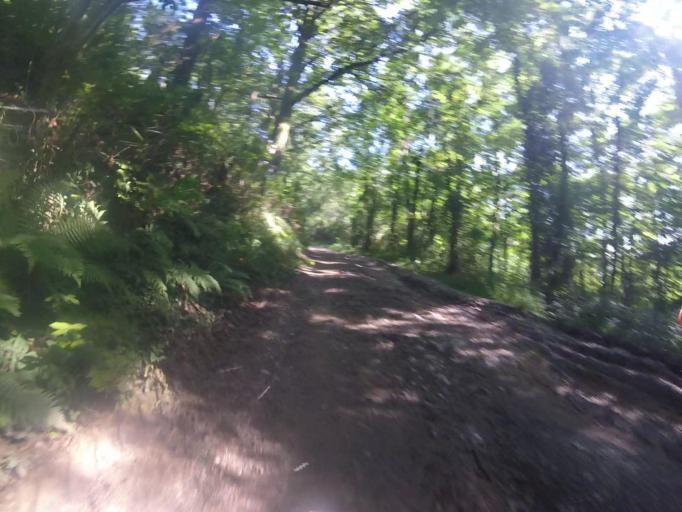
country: ES
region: Basque Country
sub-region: Provincia de Guipuzcoa
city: Astigarraga
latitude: 43.2631
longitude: -1.9362
